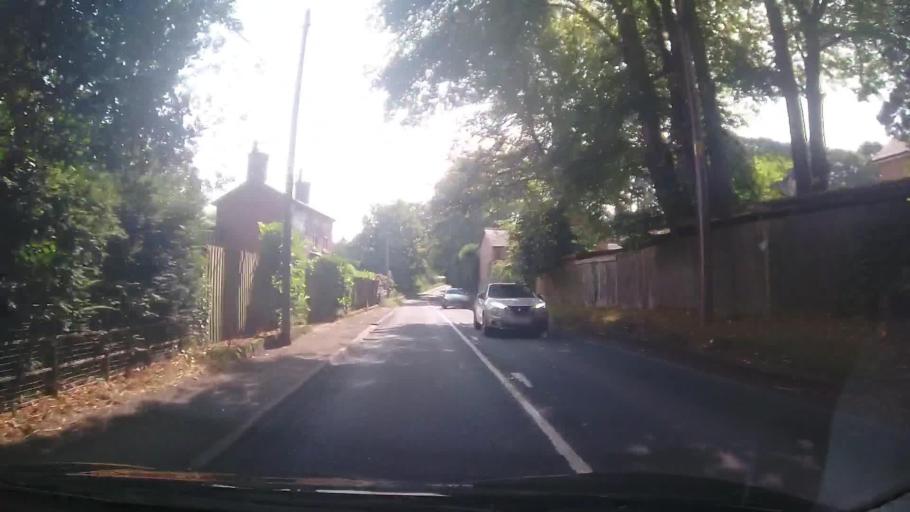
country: GB
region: England
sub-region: Cheshire West and Chester
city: Tiverton
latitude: 53.1167
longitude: -2.6610
